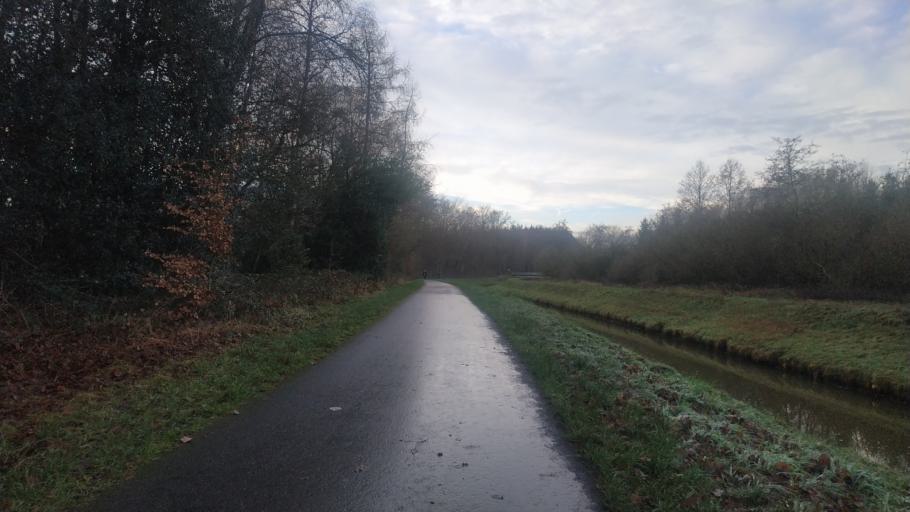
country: DE
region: North Rhine-Westphalia
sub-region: Regierungsbezirk Munster
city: Birgte
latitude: 52.2887
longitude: 7.6378
